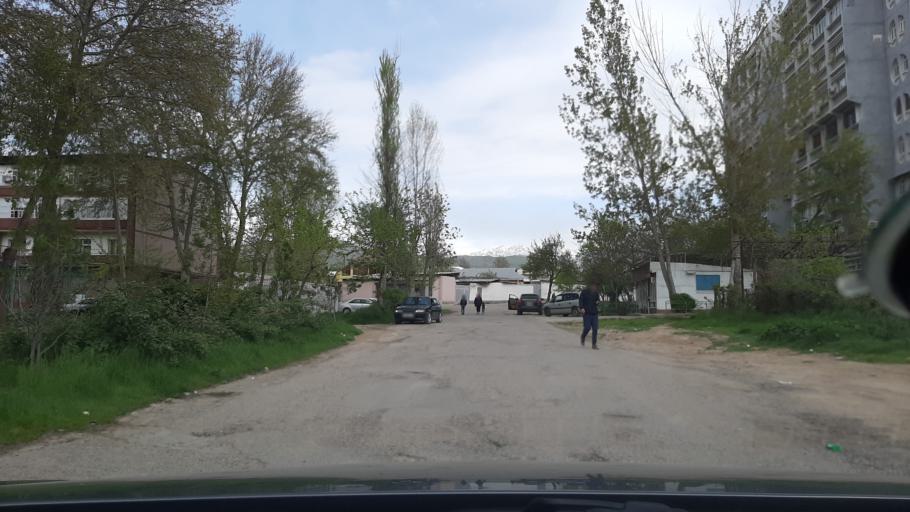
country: TJ
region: Dushanbe
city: Dushanbe
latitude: 38.5884
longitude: 68.7491
